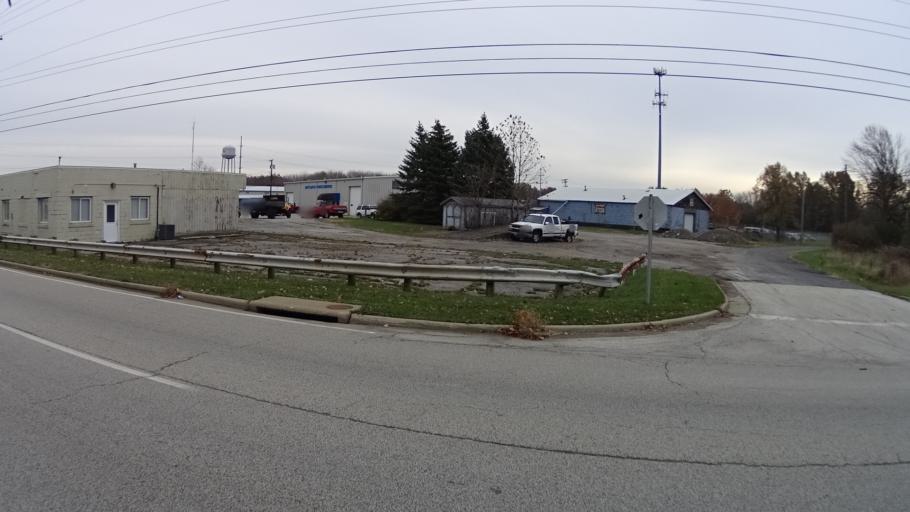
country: US
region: Ohio
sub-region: Lorain County
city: Elyria
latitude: 41.3429
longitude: -82.1170
